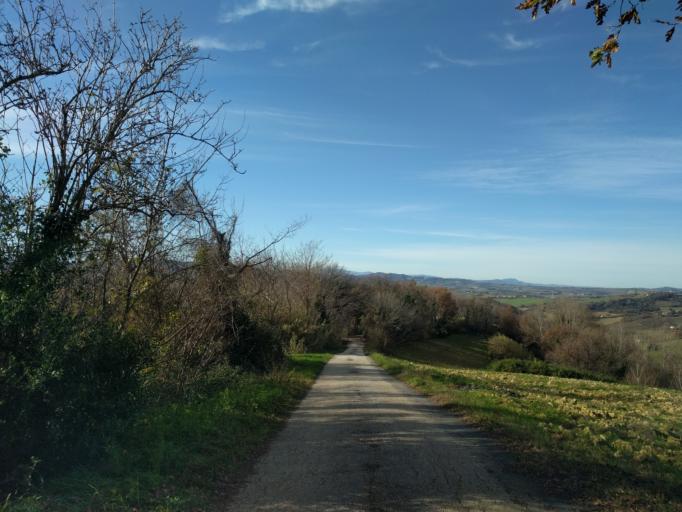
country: IT
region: The Marches
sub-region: Provincia di Pesaro e Urbino
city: Cuccurano
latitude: 43.8096
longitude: 12.9566
